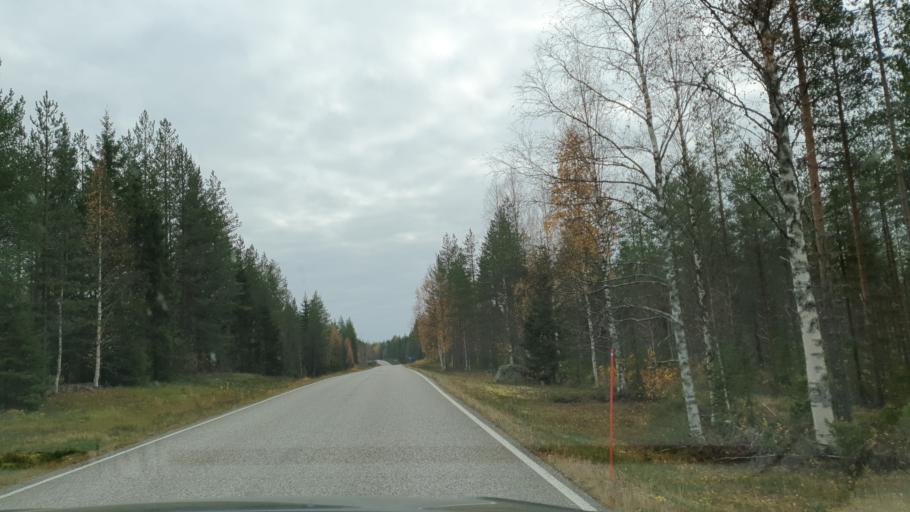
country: FI
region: Kainuu
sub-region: Kajaani
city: Ristijaervi
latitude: 64.6214
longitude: 27.9945
